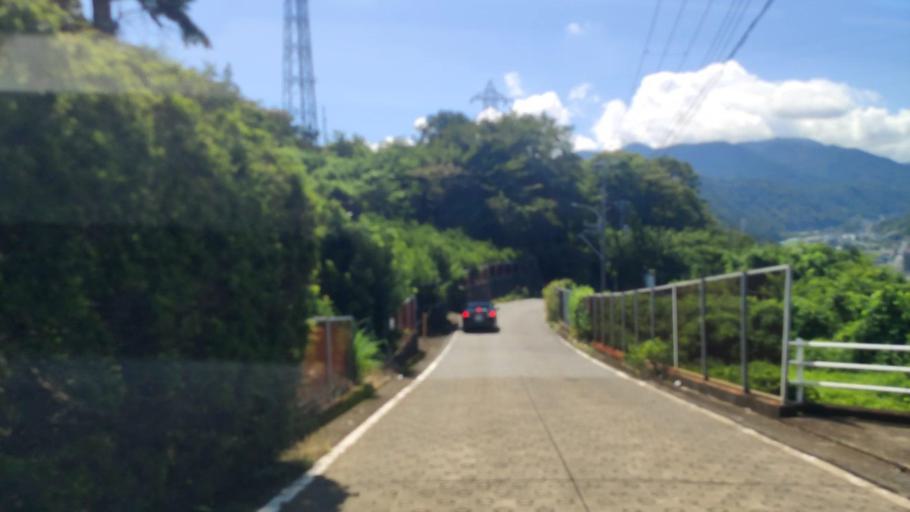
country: JP
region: Kanagawa
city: Odawara
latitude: 35.2486
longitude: 139.1347
